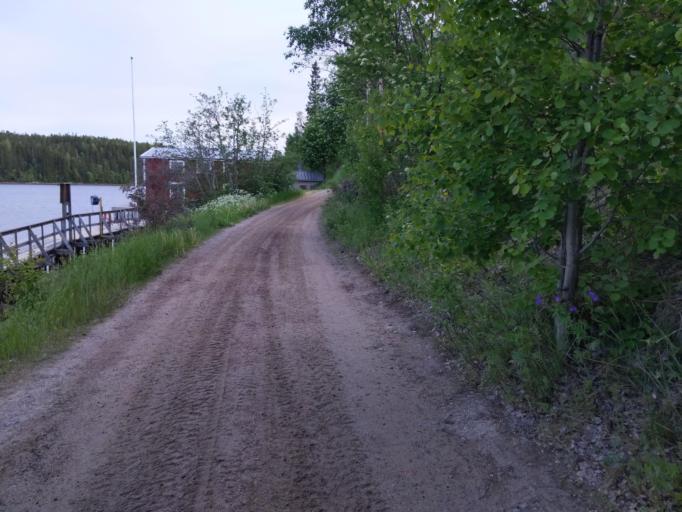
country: SE
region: Vaesternorrland
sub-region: OErnskoeldsviks Kommun
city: Kopmanholmen
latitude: 63.0199
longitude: 18.6463
